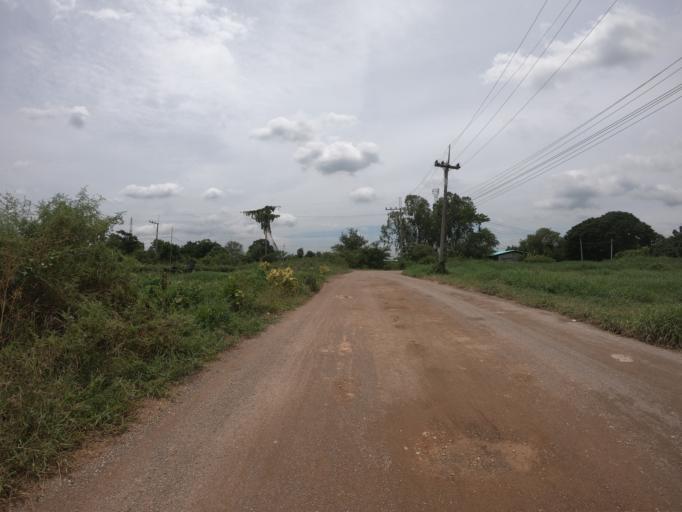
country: TH
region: Pathum Thani
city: Ban Lam Luk Ka
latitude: 13.9861
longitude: 100.8528
